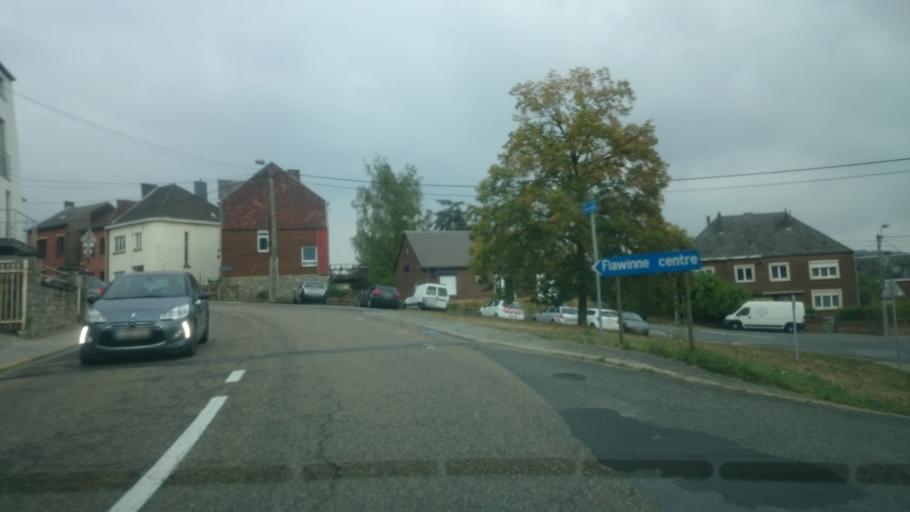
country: BE
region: Wallonia
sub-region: Province de Namur
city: Namur
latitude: 50.4558
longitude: 4.8126
